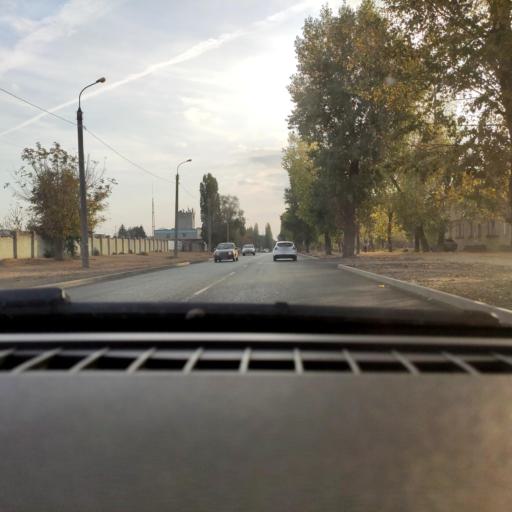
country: RU
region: Voronezj
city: Voronezh
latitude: 51.6510
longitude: 39.2455
